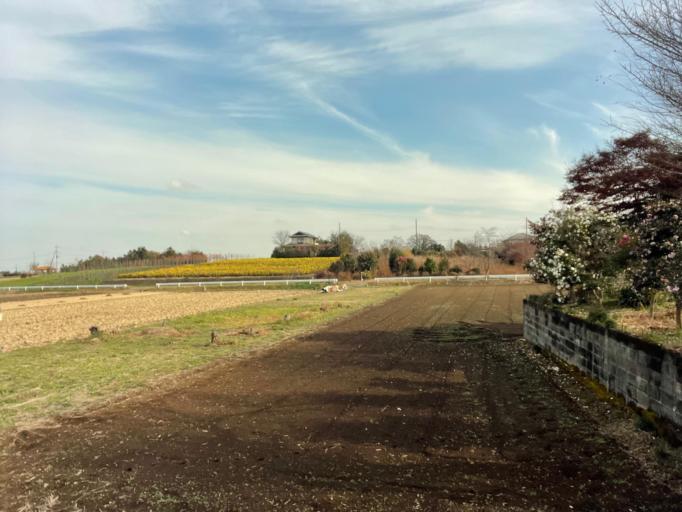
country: JP
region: Saitama
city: Yorii
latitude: 36.1476
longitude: 139.1942
